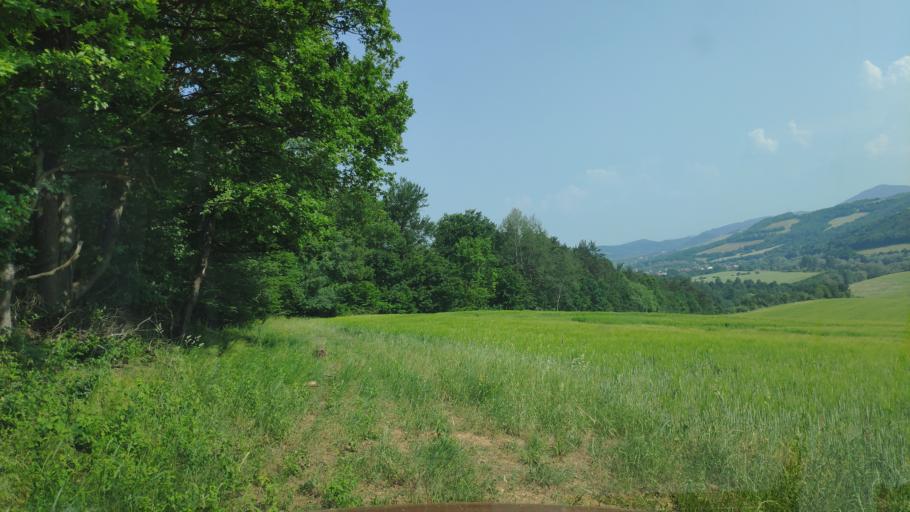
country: SK
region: Presovsky
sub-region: Okres Presov
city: Presov
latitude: 48.9649
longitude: 21.1521
